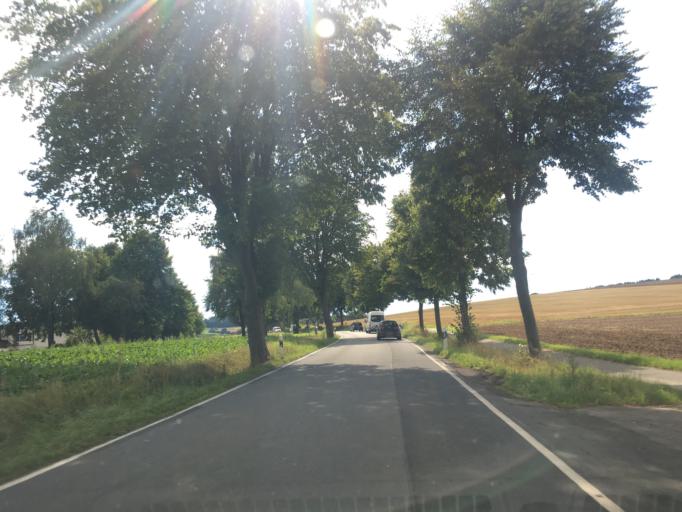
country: DE
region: North Rhine-Westphalia
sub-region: Regierungsbezirk Detmold
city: Barntrup
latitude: 51.9884
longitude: 9.0914
